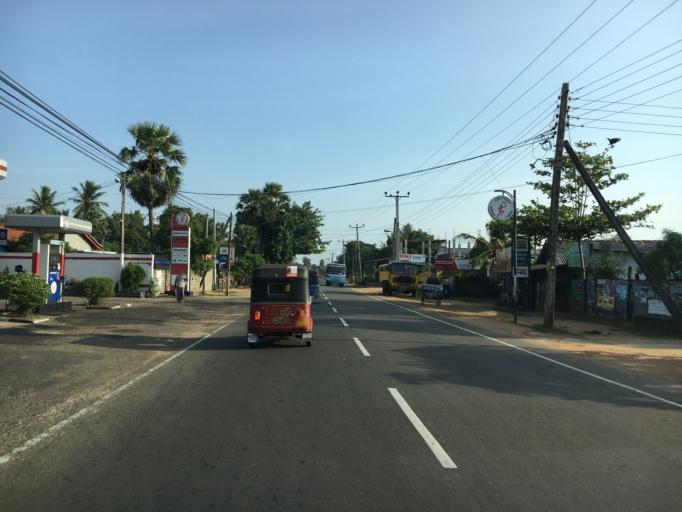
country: LK
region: Eastern Province
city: Eravur Town
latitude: 7.9245
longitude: 81.5137
